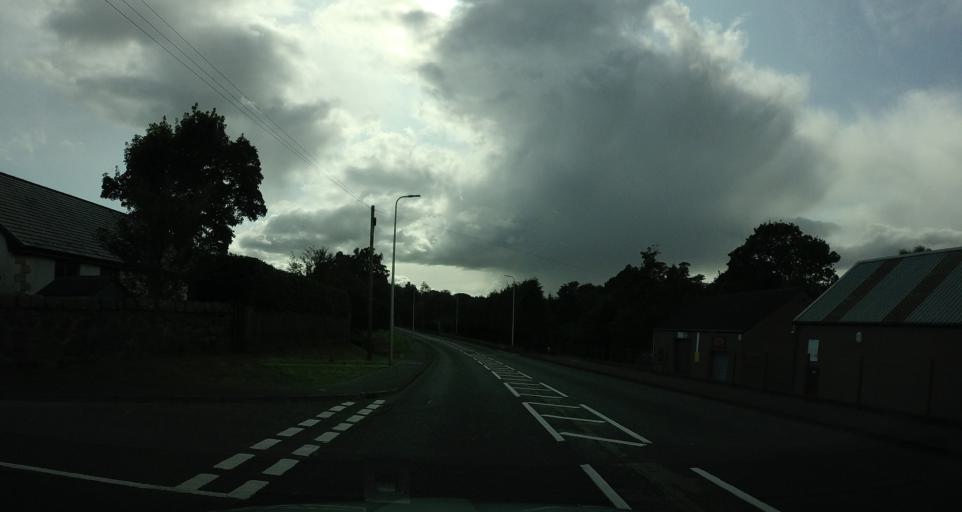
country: GB
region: Scotland
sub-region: Fife
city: Saline
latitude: 56.1833
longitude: -3.5621
